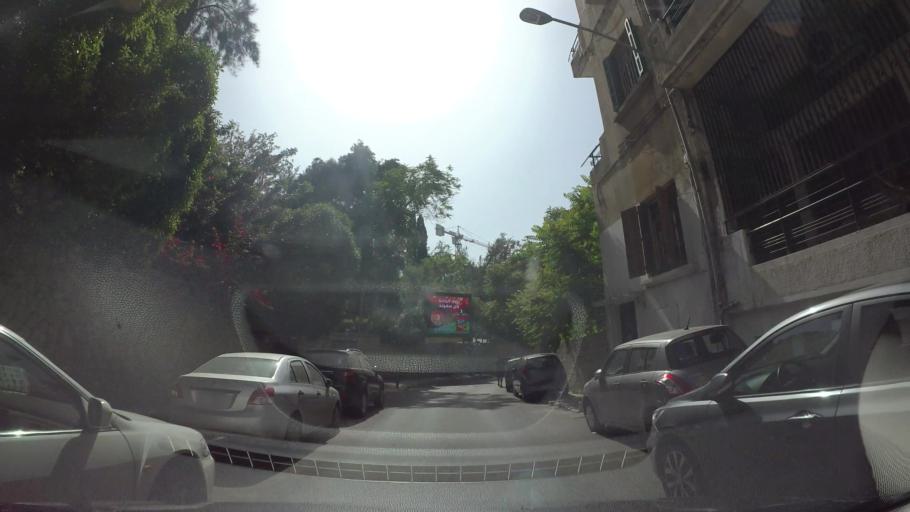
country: LB
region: Beyrouth
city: Ra's Bayrut
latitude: 33.8992
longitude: 35.4903
